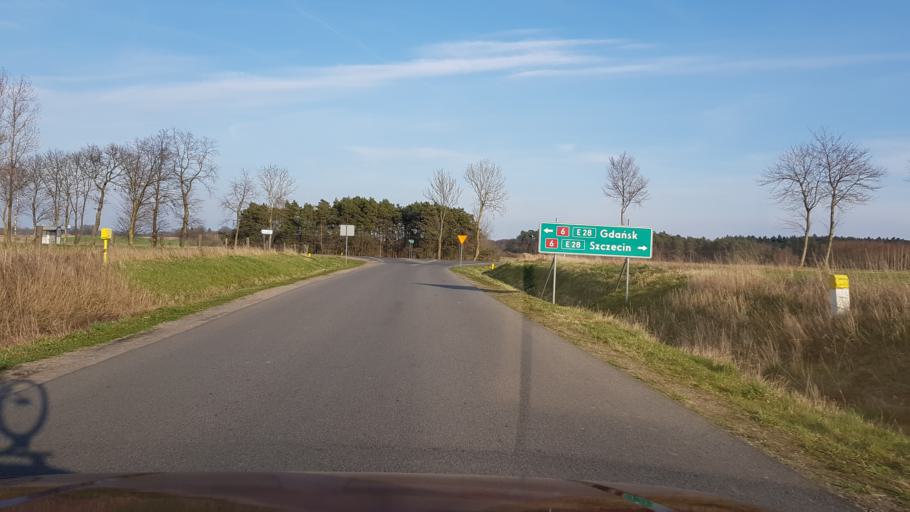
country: PL
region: West Pomeranian Voivodeship
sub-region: Powiat bialogardzki
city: Bialogard
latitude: 54.1206
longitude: 16.0077
